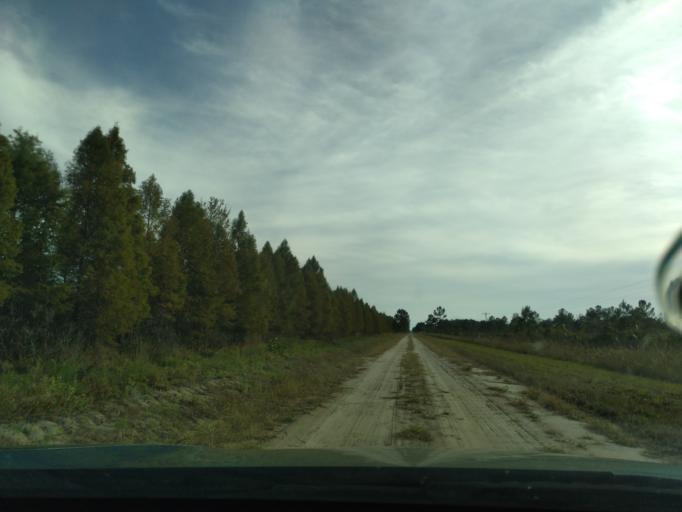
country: US
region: North Carolina
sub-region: Beaufort County
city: Belhaven
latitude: 35.6813
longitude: -76.5451
